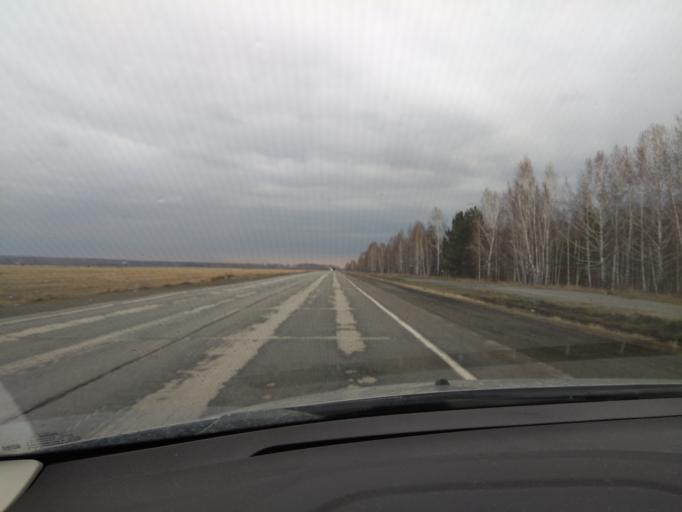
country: RU
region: Chelyabinsk
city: Tyubuk
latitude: 55.9728
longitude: 61.0476
